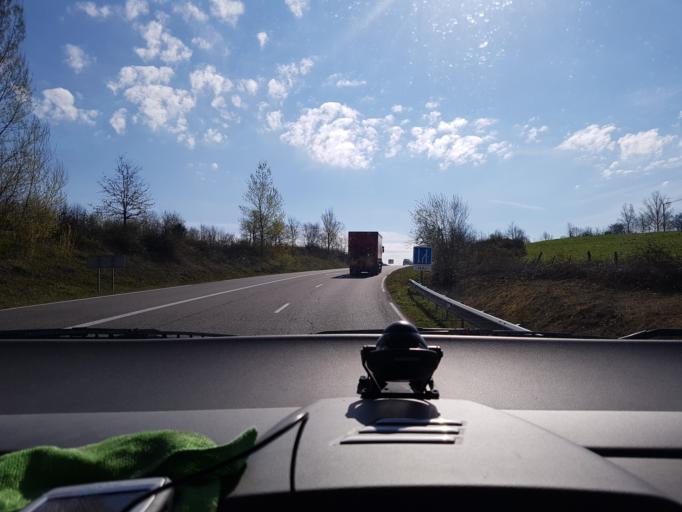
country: FR
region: Midi-Pyrenees
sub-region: Departement de l'Aveyron
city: Moyrazes
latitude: 44.3815
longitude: 2.4475
